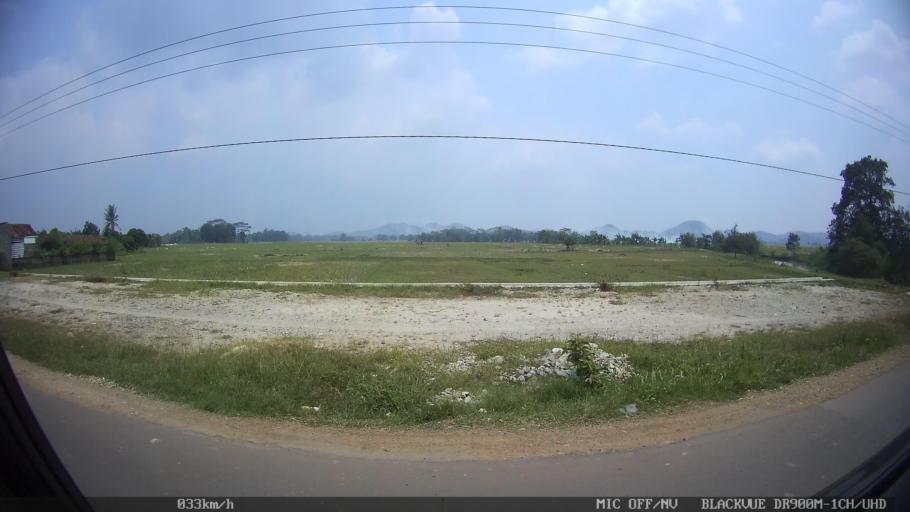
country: ID
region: Lampung
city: Pringsewu
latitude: -5.3532
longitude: 105.0149
